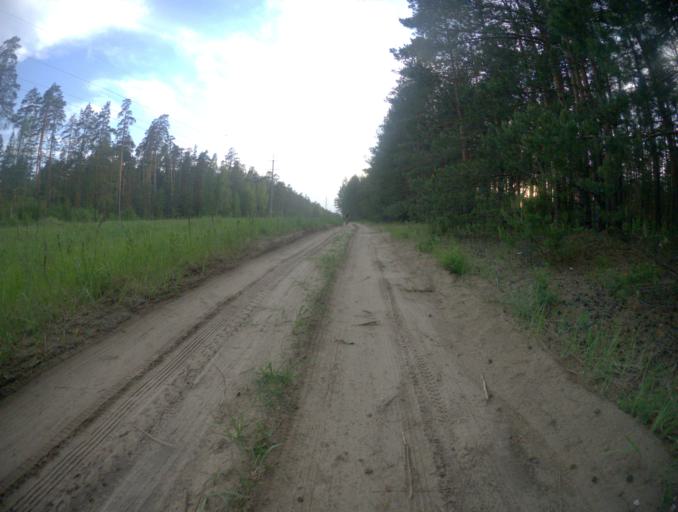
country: RU
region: Vladimir
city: Gus'-Khrustal'nyy
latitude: 55.6330
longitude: 40.6876
